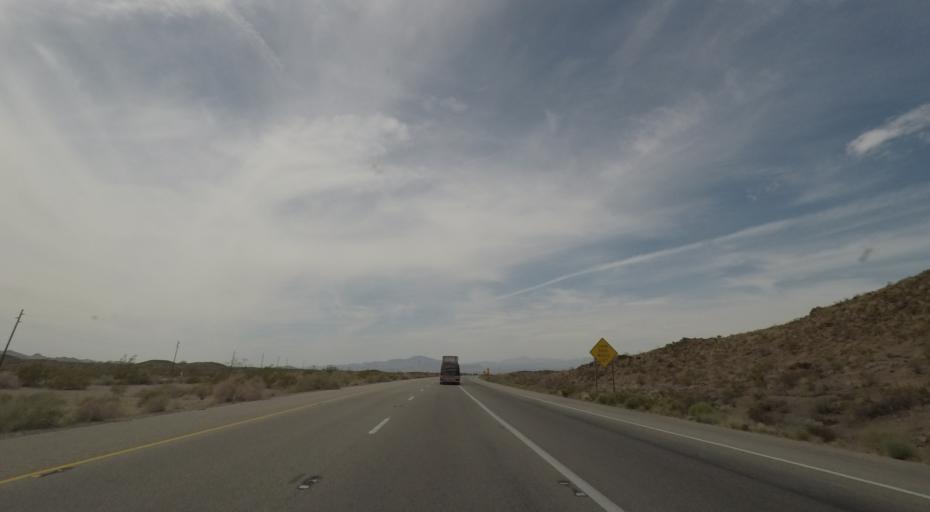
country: US
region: California
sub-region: San Bernardino County
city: Needles
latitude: 34.8292
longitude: -115.0576
